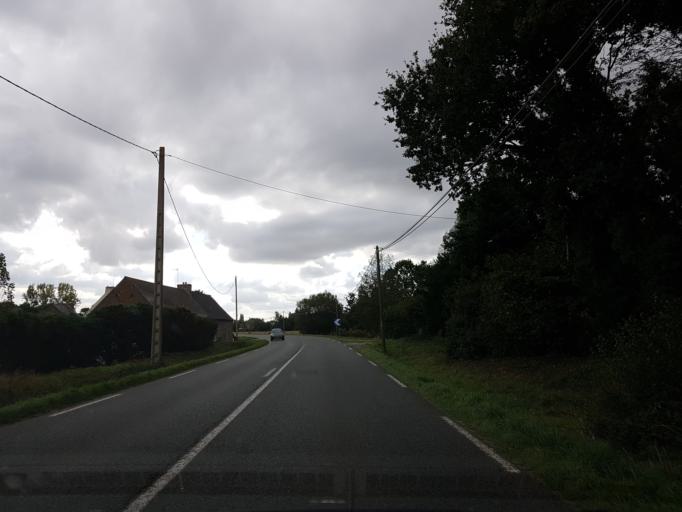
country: FR
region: Brittany
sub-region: Departement des Cotes-d'Armor
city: Pommeret
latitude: 48.4601
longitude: -2.6510
